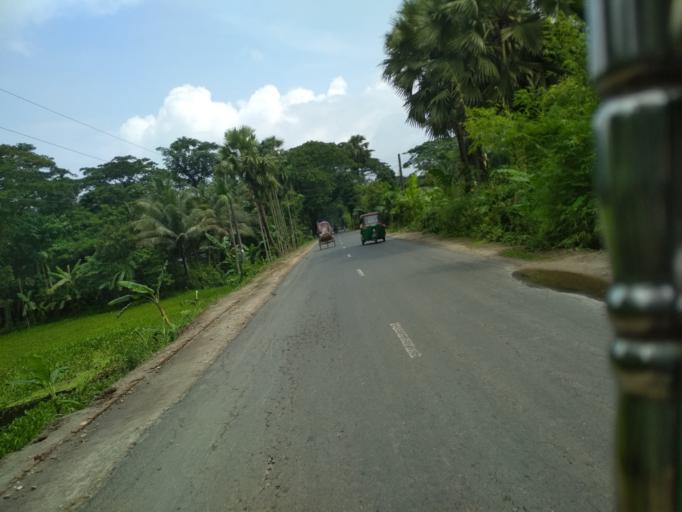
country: BD
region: Chittagong
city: Lakshmipur
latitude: 22.9574
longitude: 90.8092
